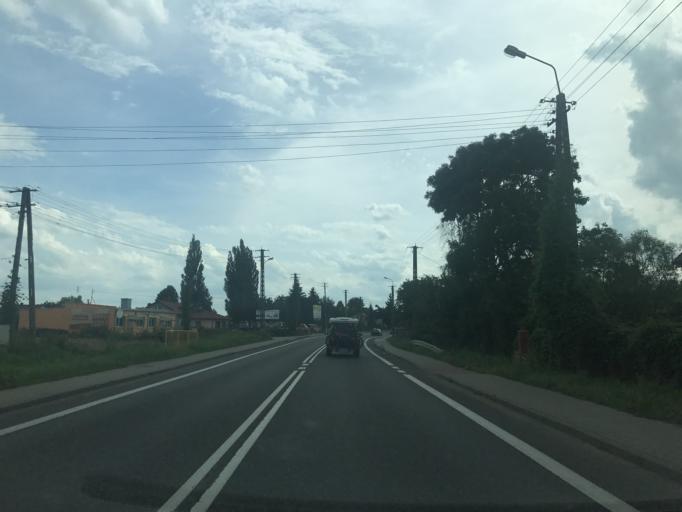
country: PL
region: Masovian Voivodeship
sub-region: Powiat mlawski
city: Wisniewo
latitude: 52.9993
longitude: 20.3297
